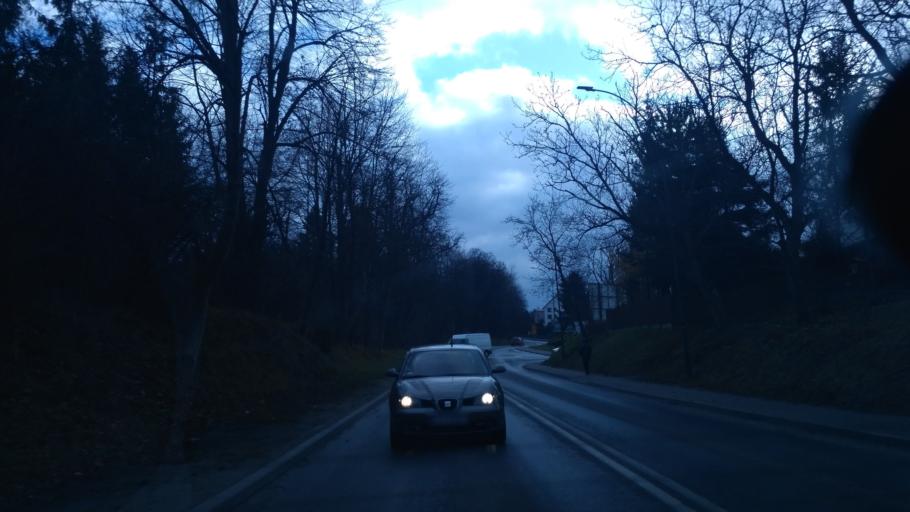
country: PL
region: Subcarpathian Voivodeship
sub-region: Powiat lancucki
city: Lancut
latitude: 50.0791
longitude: 22.2334
